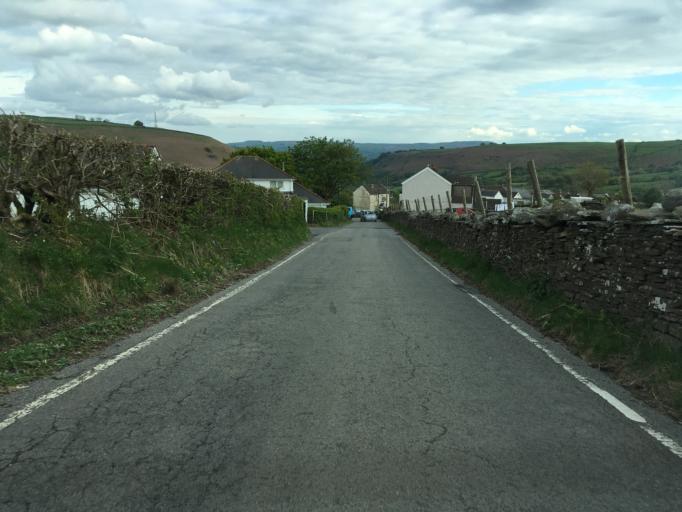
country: GB
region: Wales
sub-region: Merthyr Tydfil County Borough
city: Treharris
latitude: 51.7074
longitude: -3.3109
